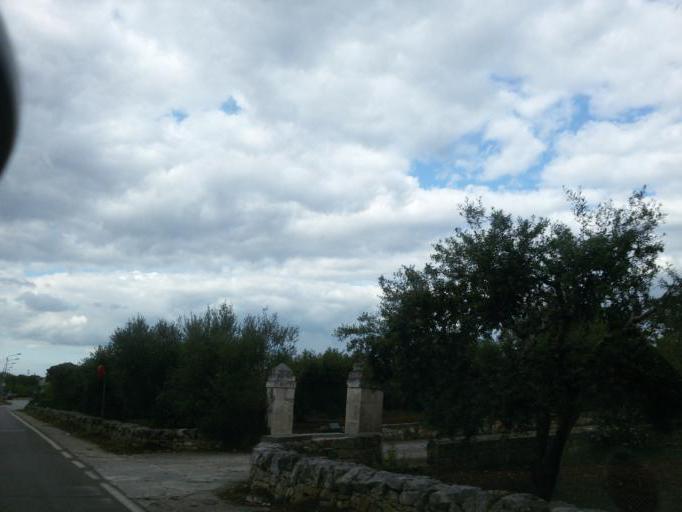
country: IT
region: Apulia
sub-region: Provincia di Bari
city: Locorotondo
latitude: 40.7627
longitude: 17.3308
